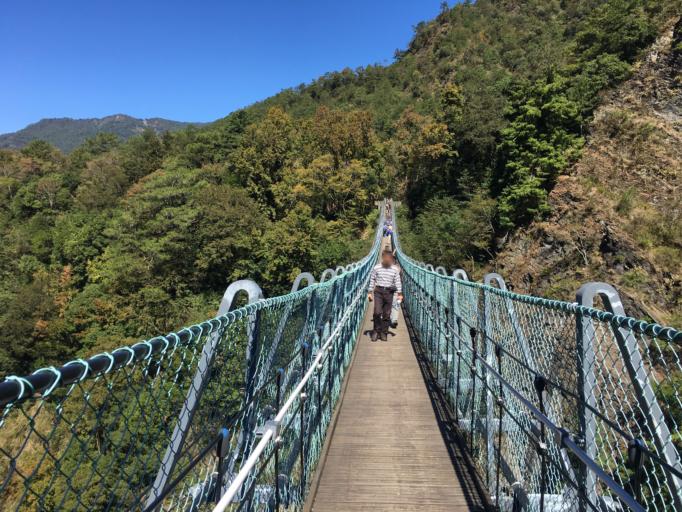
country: TW
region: Taiwan
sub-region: Nantou
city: Puli
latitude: 23.9449
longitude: 121.1912
